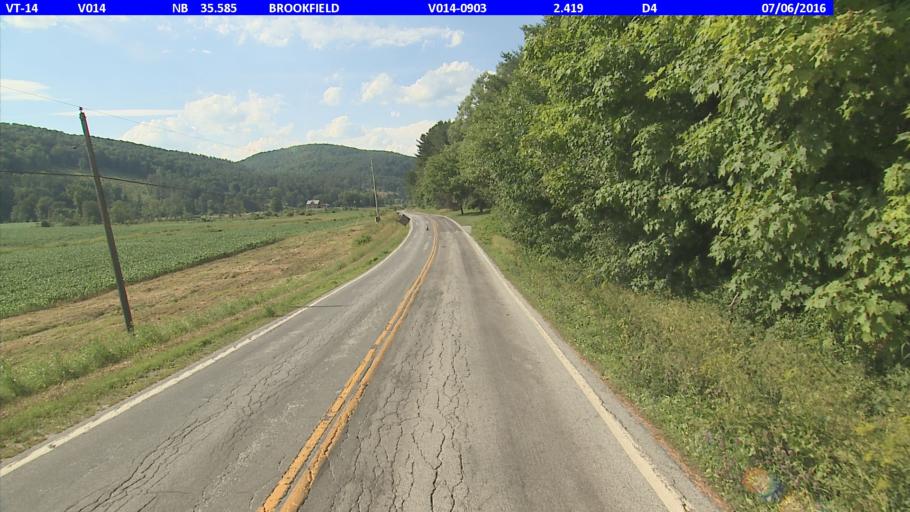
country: US
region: Vermont
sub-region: Orange County
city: Williamstown
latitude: 44.0121
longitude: -72.5677
